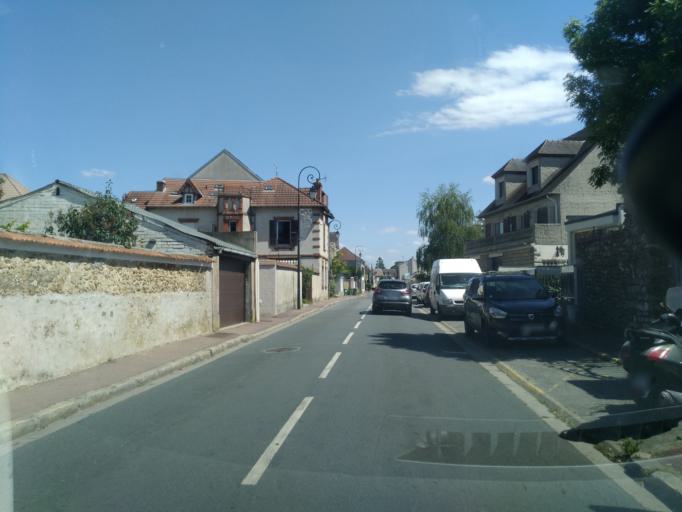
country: FR
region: Ile-de-France
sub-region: Departement des Yvelines
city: Neauphle-le-Chateau
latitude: 48.8153
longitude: 1.9003
